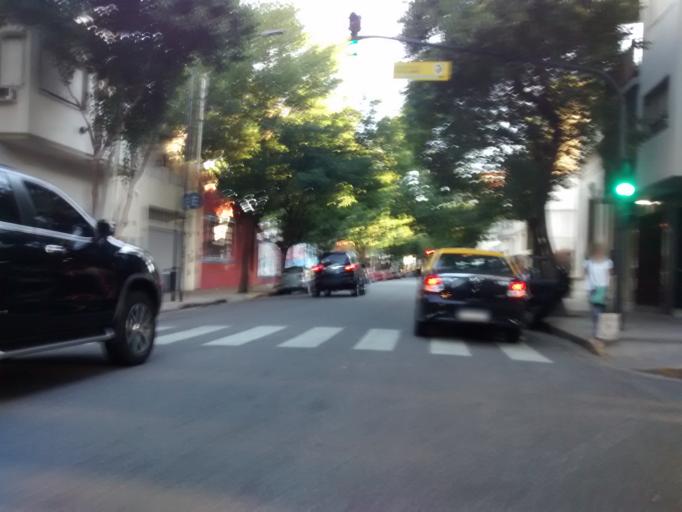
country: AR
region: Buenos Aires F.D.
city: Villa Santa Rita
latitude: -34.6128
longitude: -58.4448
